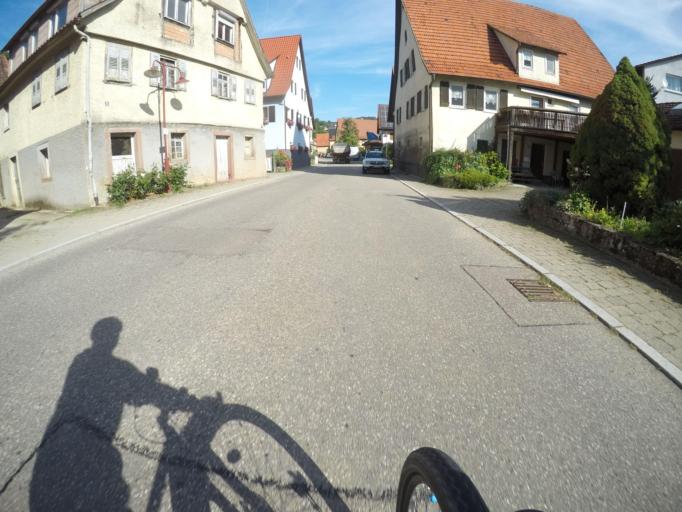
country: DE
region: Baden-Wuerttemberg
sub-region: Karlsruhe Region
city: Monsheim
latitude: 48.8842
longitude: 8.8992
